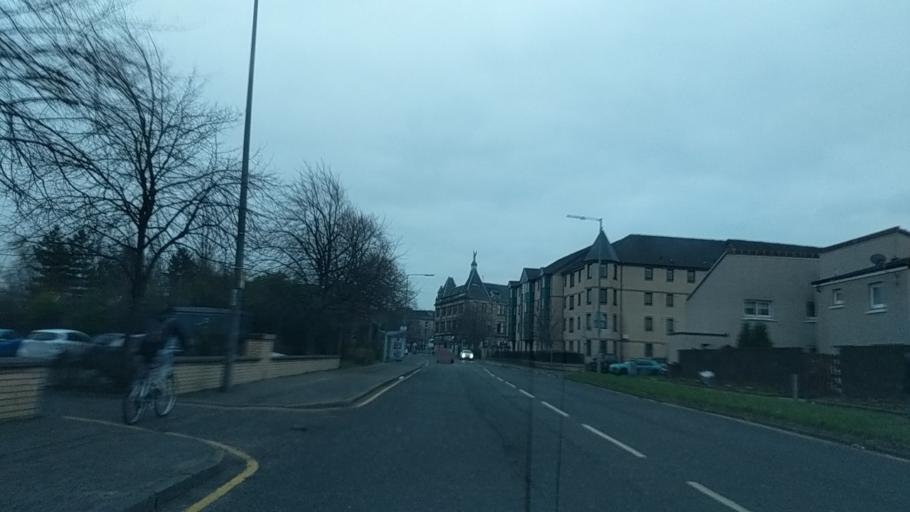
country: GB
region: Scotland
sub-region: Glasgow City
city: Glasgow
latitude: 55.8549
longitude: -4.2818
